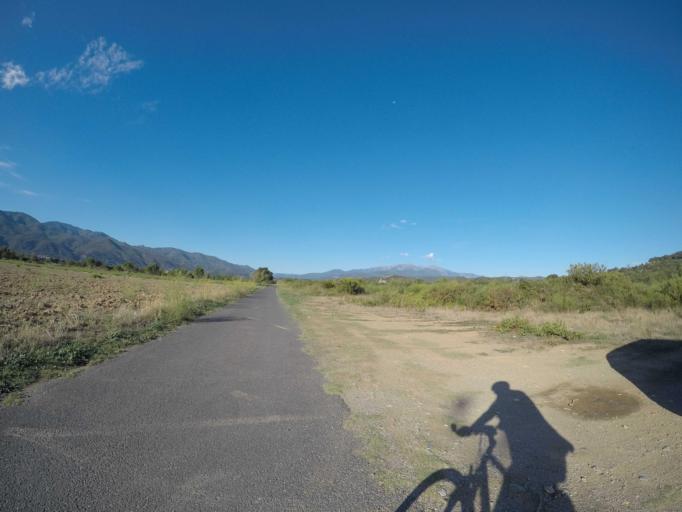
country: FR
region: Languedoc-Roussillon
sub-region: Departement des Pyrenees-Orientales
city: Sant Joan de Pladecorts
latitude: 42.5143
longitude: 2.7799
